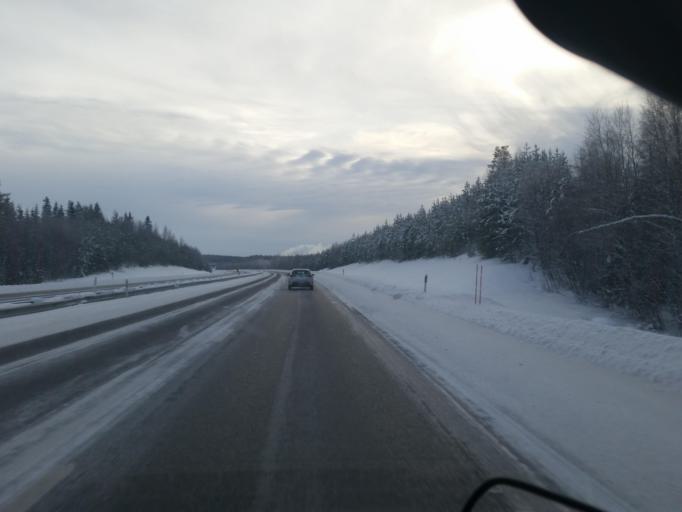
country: SE
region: Norrbotten
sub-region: Pitea Kommun
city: Norrfjarden
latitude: 65.3647
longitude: 21.4300
